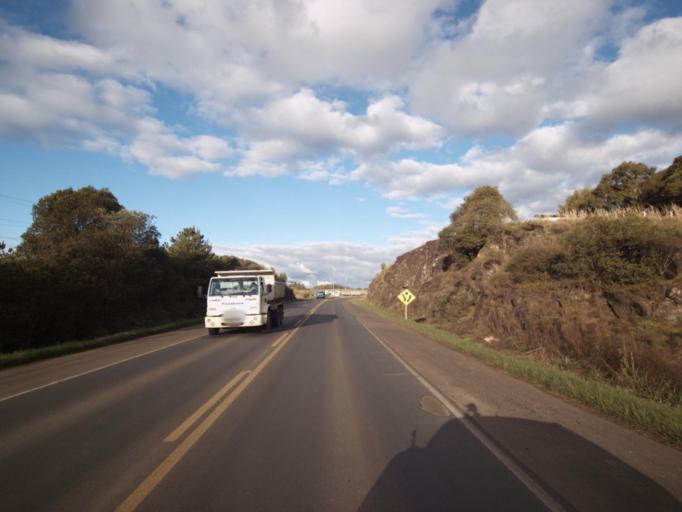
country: BR
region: Santa Catarina
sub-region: Campos Novos
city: Campos Novos
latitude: -27.3929
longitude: -51.1946
